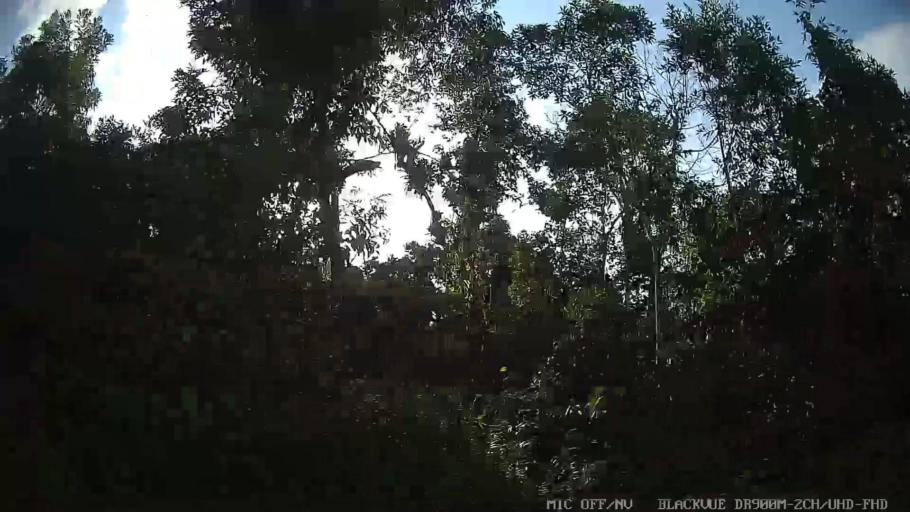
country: BR
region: Sao Paulo
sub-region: Itanhaem
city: Itanhaem
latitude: -24.1480
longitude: -46.8123
